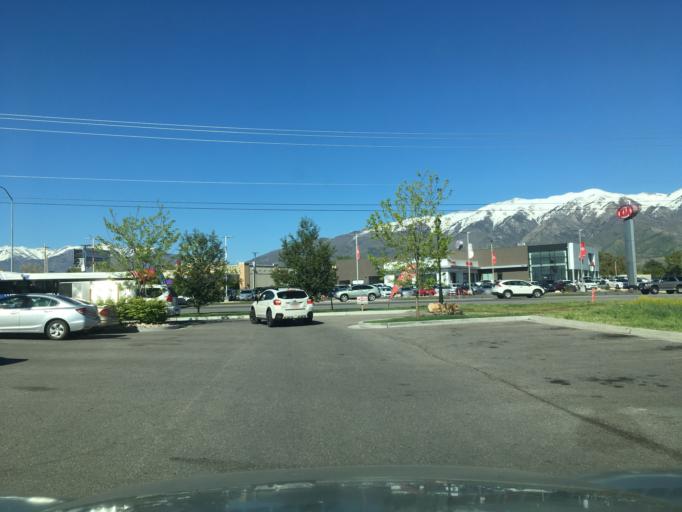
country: US
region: Utah
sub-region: Davis County
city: Layton
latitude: 41.0661
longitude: -111.9727
